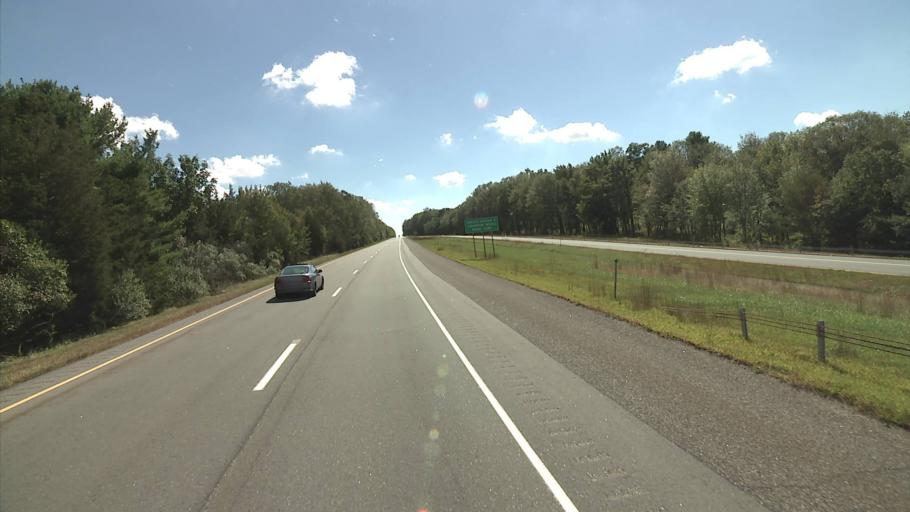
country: US
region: Connecticut
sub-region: New London County
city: Colchester
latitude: 41.5569
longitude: -72.3215
